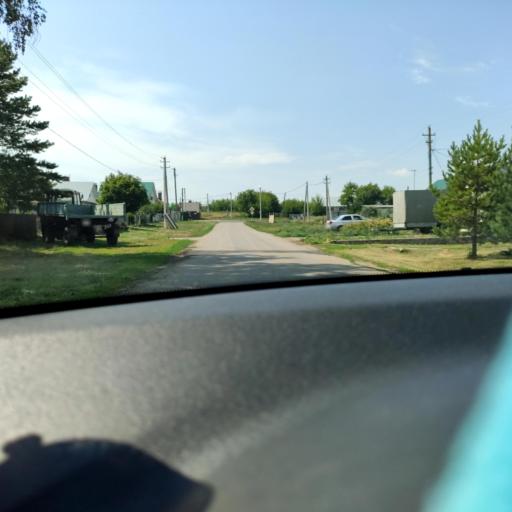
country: RU
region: Samara
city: Kinel'
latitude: 53.3417
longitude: 50.5194
